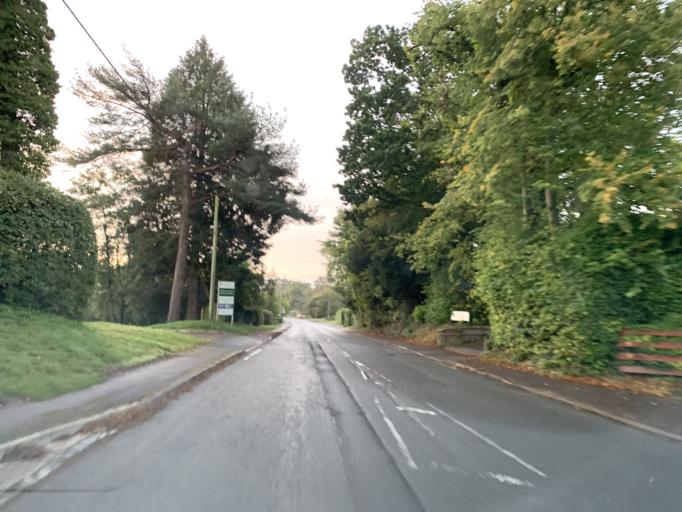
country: GB
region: England
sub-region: Wiltshire
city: Alderbury
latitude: 51.0424
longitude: -1.7313
